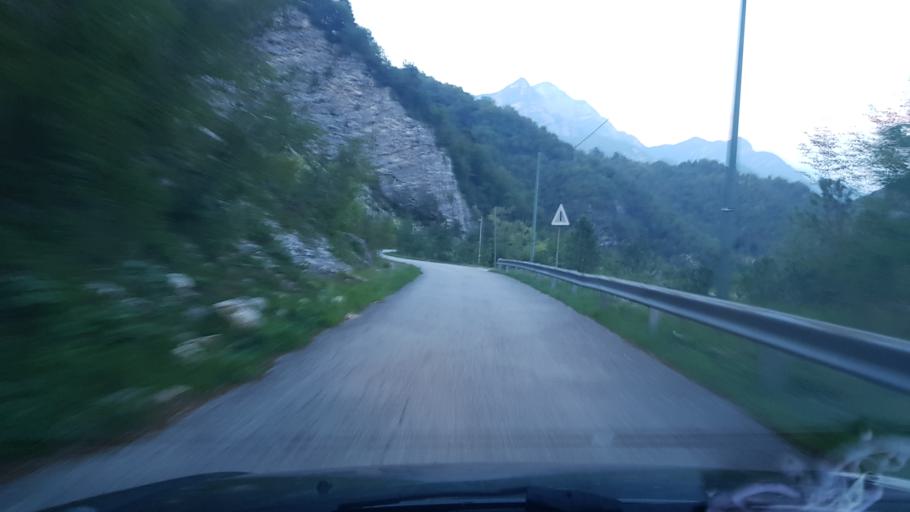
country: IT
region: Friuli Venezia Giulia
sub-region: Provincia di Pordenone
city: Frisanco
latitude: 46.2528
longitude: 12.7071
